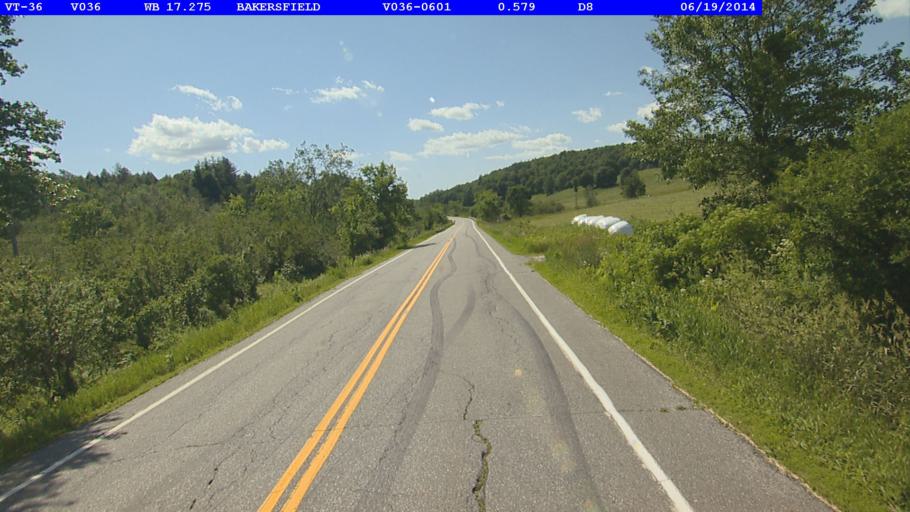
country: US
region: Vermont
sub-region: Franklin County
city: Enosburg Falls
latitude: 44.7848
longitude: -72.8383
